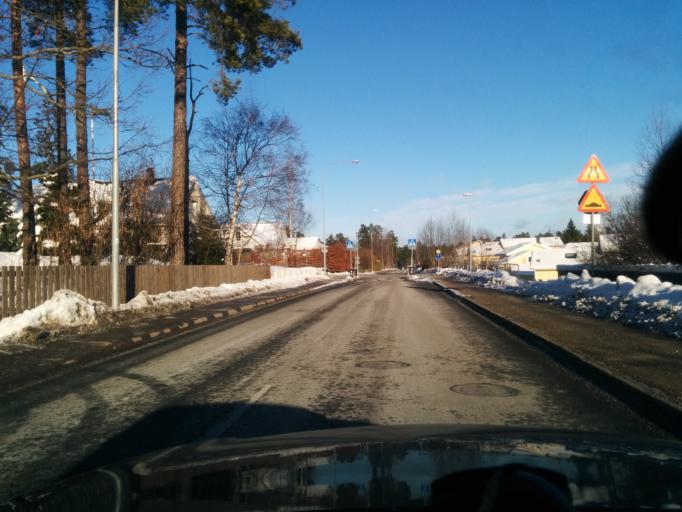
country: SE
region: Stockholm
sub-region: Taby Kommun
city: Taby
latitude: 59.4666
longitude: 18.0898
